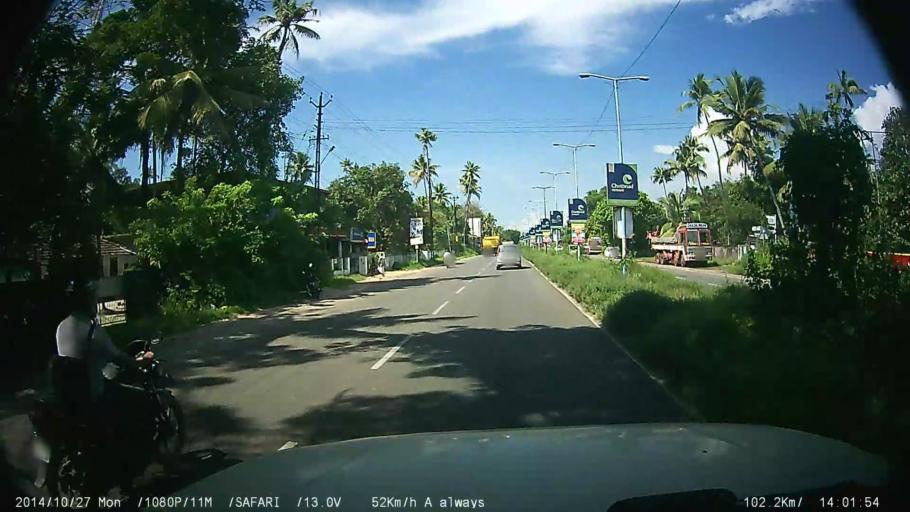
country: IN
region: Kerala
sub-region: Alappuzha
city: Vayalar
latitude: 9.7041
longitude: 76.3171
